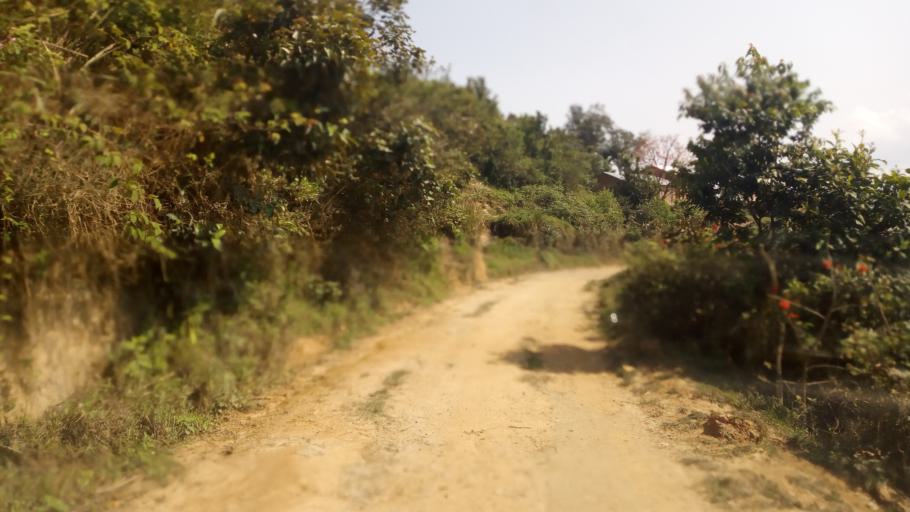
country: UG
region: Western Region
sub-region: Kisoro District
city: Kisoro
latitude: -1.1117
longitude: 29.5927
